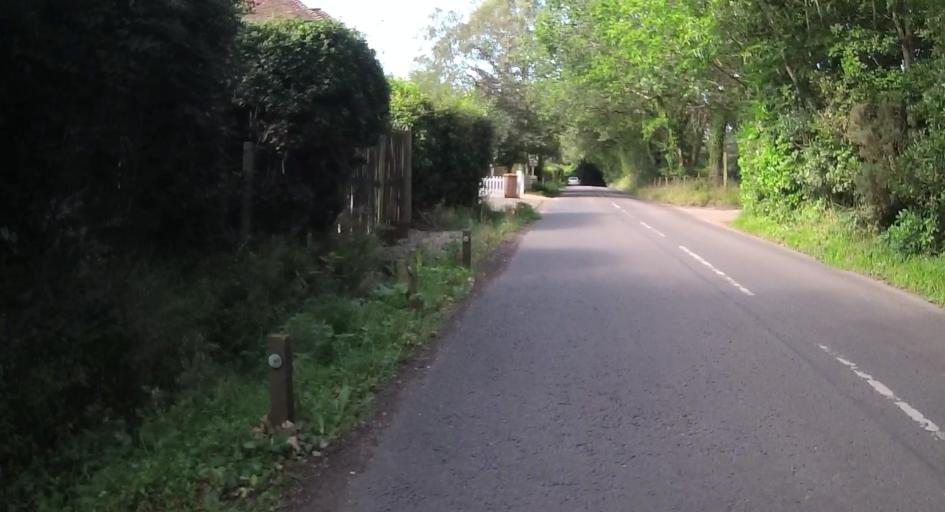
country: GB
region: England
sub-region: Surrey
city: Farnham
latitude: 51.1800
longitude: -0.7999
